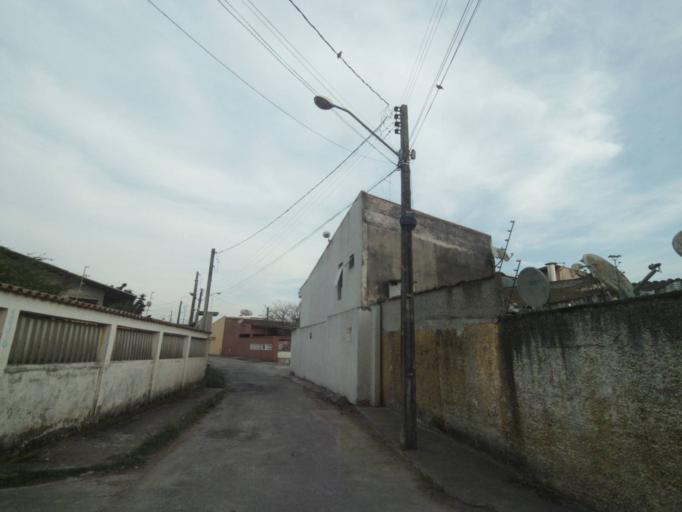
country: BR
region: Parana
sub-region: Paranagua
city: Paranagua
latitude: -25.5254
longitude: -48.5343
